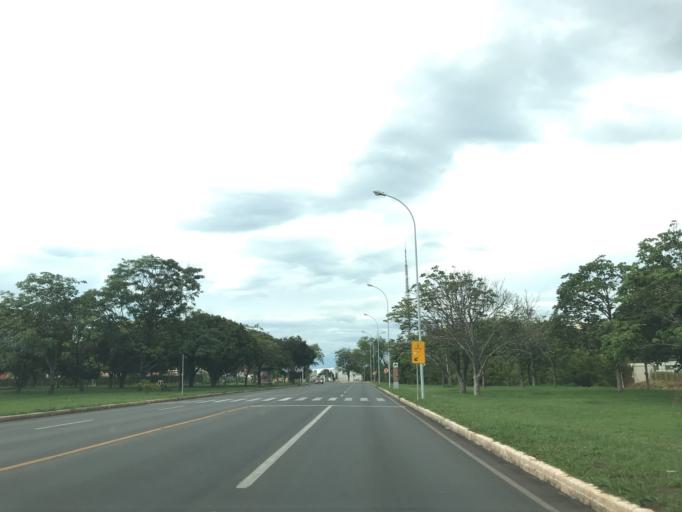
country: BR
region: Federal District
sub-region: Brasilia
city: Brasilia
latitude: -15.7967
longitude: -47.8991
